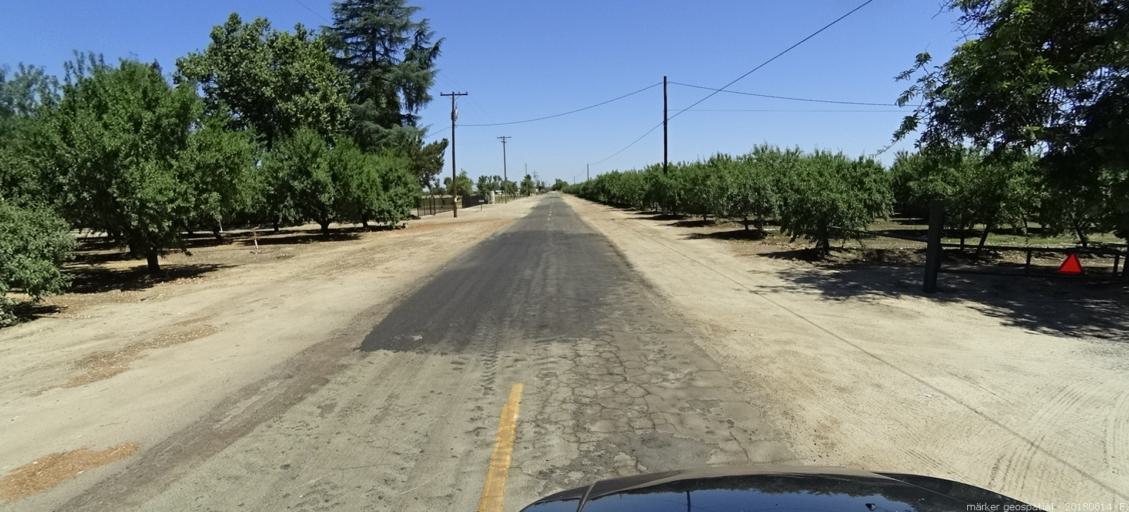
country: US
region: California
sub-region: Madera County
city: Fairmead
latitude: 36.9912
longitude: -120.1842
